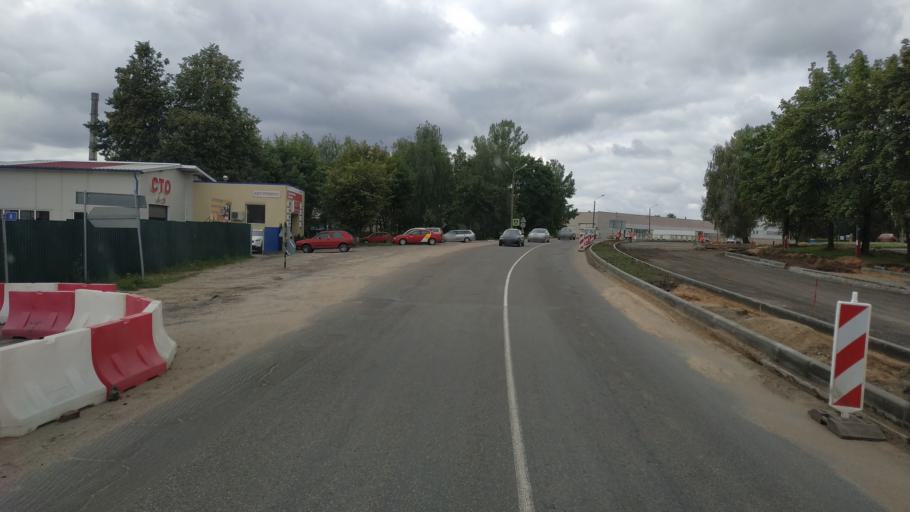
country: BY
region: Mogilev
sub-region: Mahilyowski Rayon
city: Veyno
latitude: 53.8796
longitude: 30.4104
